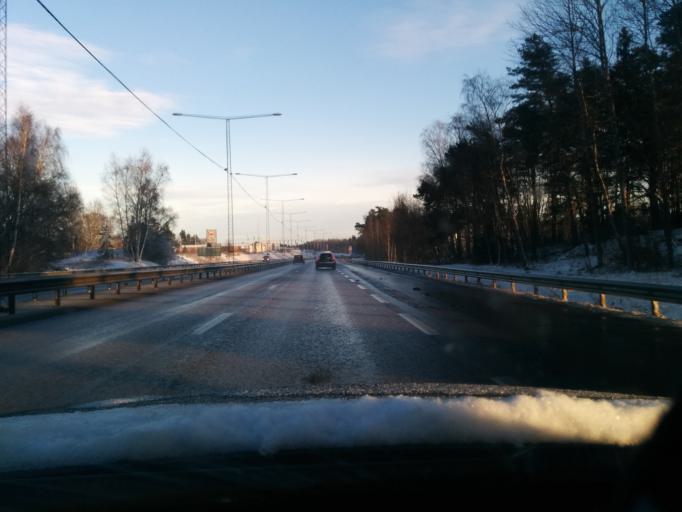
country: SE
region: Stockholm
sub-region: Danderyds Kommun
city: Djursholm
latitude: 59.4188
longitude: 18.0417
